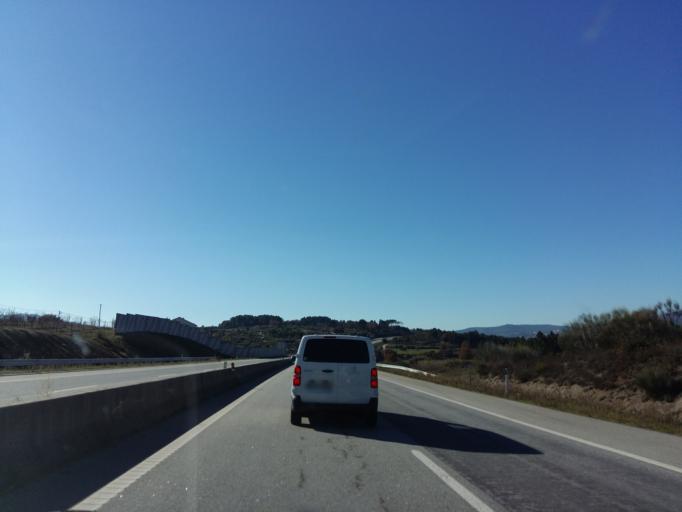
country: PT
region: Castelo Branco
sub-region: Covilha
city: Covilha
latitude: 40.2495
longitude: -7.4546
